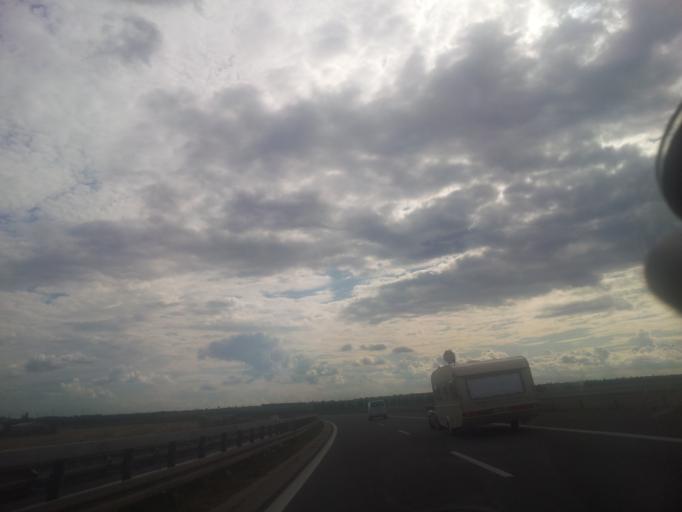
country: DE
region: Saxony-Anhalt
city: Gusten
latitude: 51.8052
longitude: 11.5966
